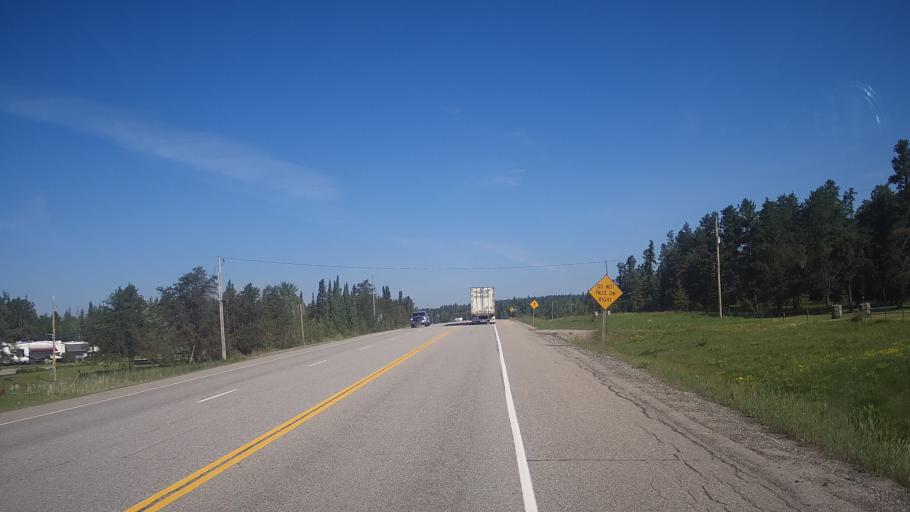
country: CA
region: Ontario
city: Dryden
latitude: 49.7150
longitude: -92.5935
